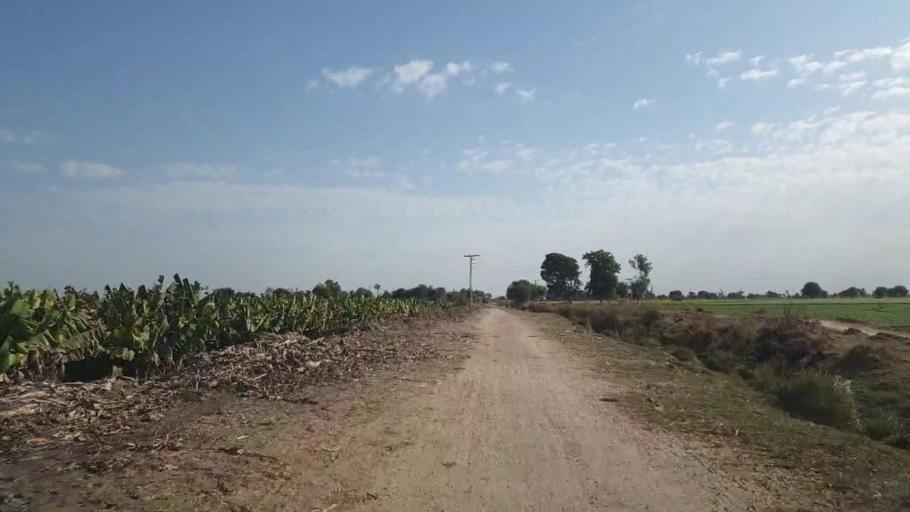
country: PK
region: Sindh
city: Shahdadpur
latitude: 26.0146
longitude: 68.4984
